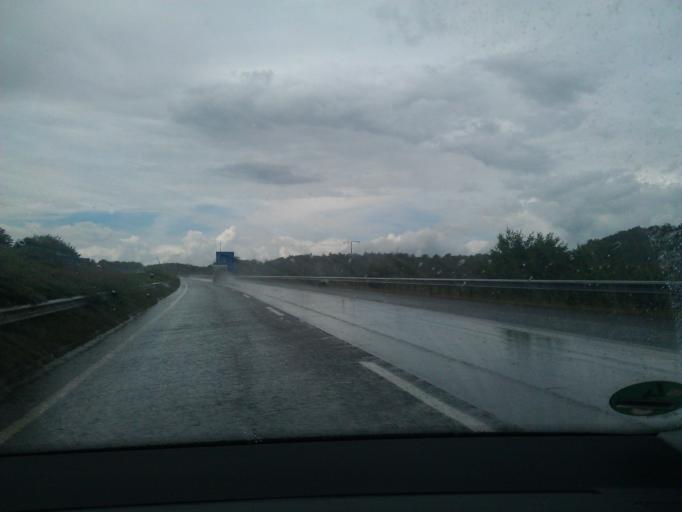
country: DE
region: Rheinland-Pfalz
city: Malbergweich
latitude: 50.0336
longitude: 6.5445
